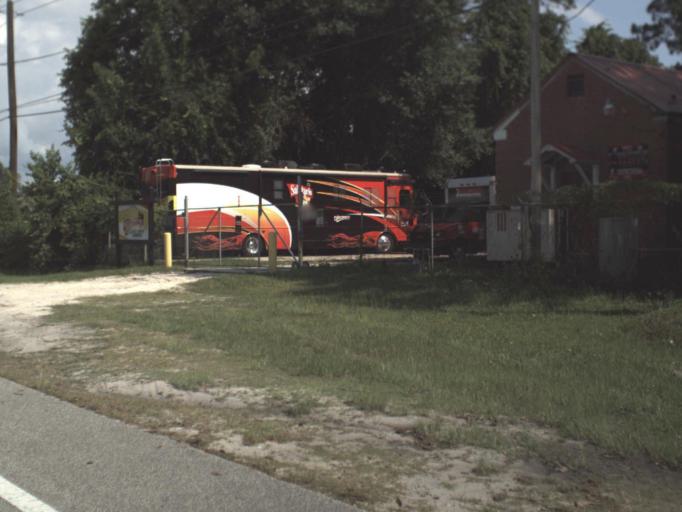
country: US
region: Florida
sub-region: Putnam County
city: Palatka
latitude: 29.6598
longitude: -81.6735
